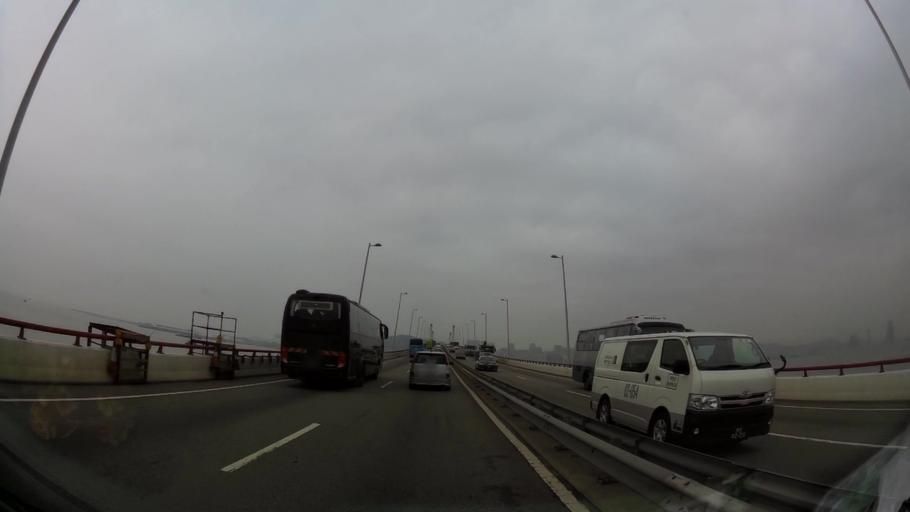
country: MO
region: Macau
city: Macau
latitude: 22.1847
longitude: 113.5634
